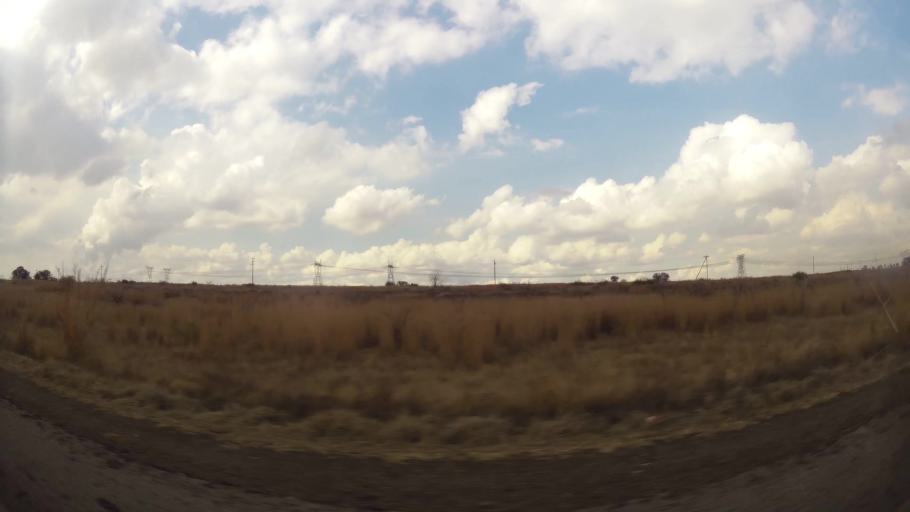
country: ZA
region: Orange Free State
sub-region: Fezile Dabi District Municipality
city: Sasolburg
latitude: -26.7930
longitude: 27.9168
